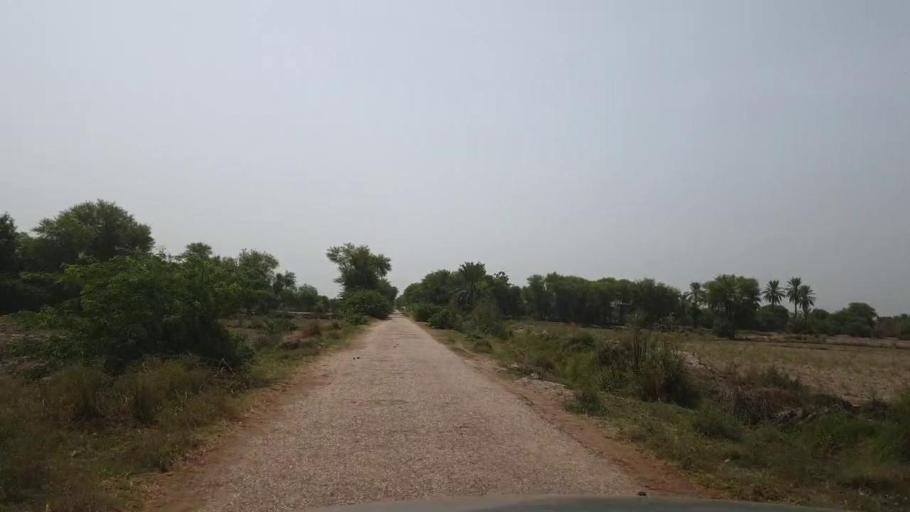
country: PK
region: Sindh
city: Madeji
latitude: 27.8268
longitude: 68.4325
